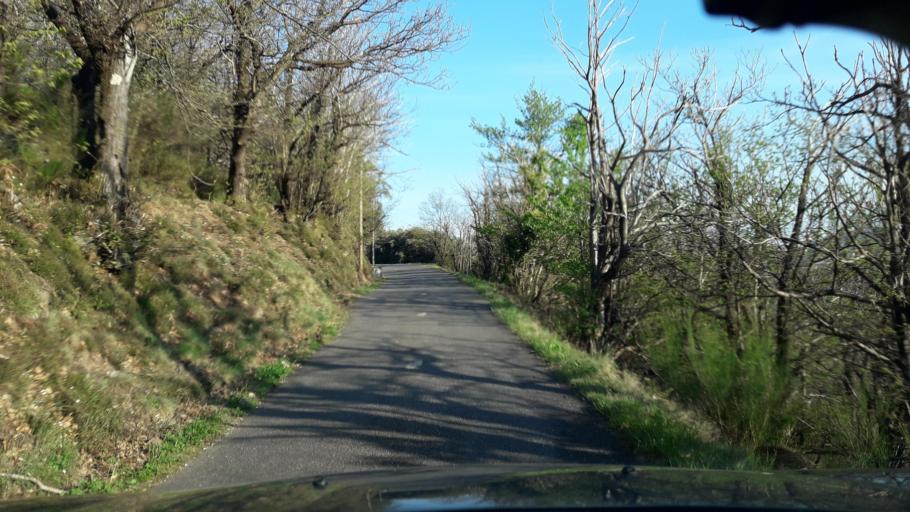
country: FR
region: Languedoc-Roussillon
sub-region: Departement du Gard
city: Valleraugue
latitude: 44.1005
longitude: 3.6362
